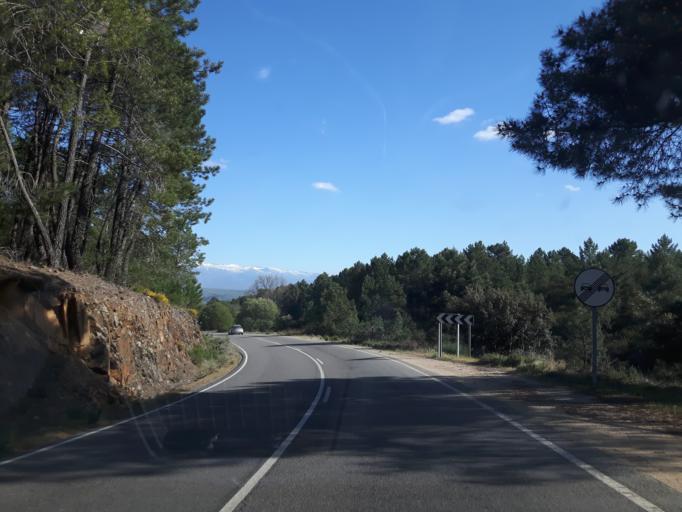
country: ES
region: Castille and Leon
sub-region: Provincia de Salamanca
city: San Miguel de Valero
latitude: 40.5323
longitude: -5.9223
